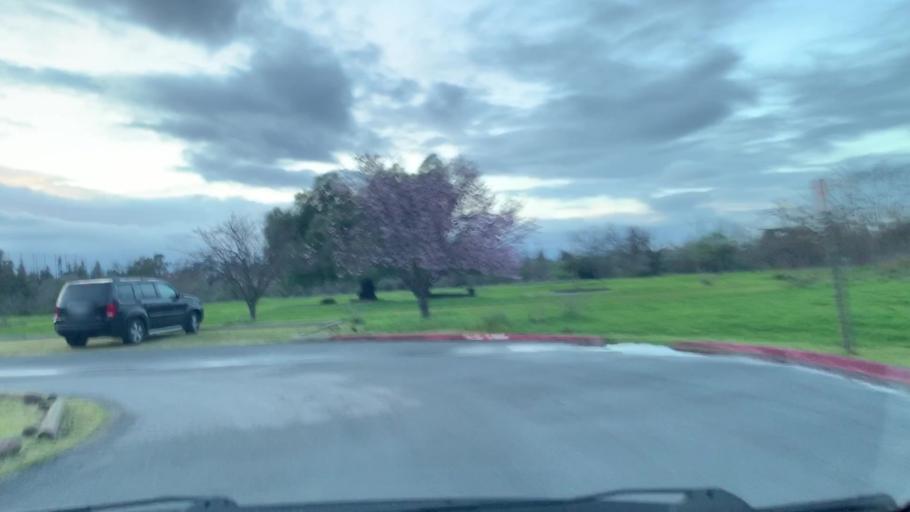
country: US
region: California
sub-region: Santa Clara County
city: Seven Trees
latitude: 37.3213
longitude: -121.8556
